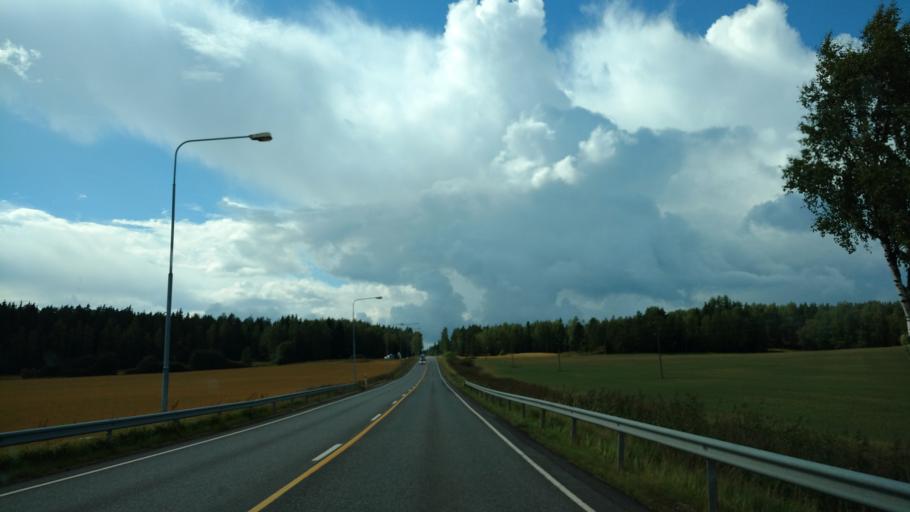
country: FI
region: Varsinais-Suomi
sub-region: Turku
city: Paimio
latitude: 60.4189
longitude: 22.7505
